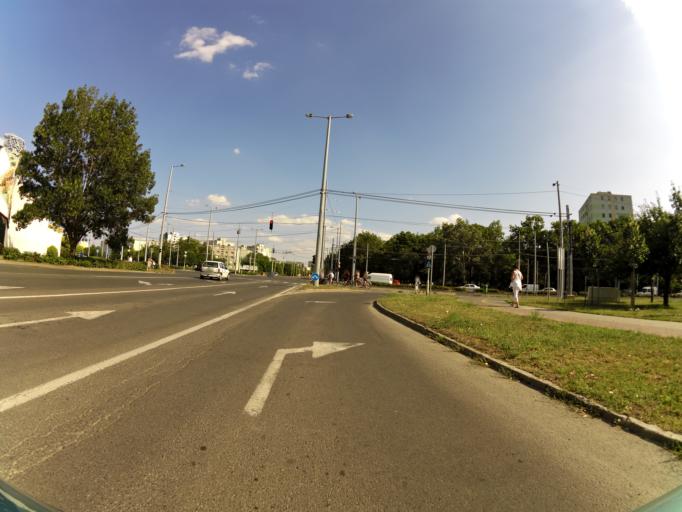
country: HU
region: Csongrad
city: Szeged
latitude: 46.2728
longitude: 20.1479
